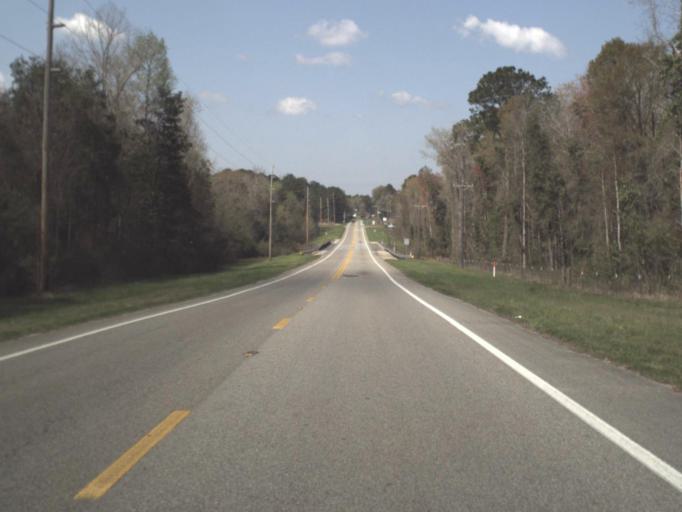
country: US
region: Florida
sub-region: Liberty County
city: Bristol
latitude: 30.3886
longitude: -84.7869
